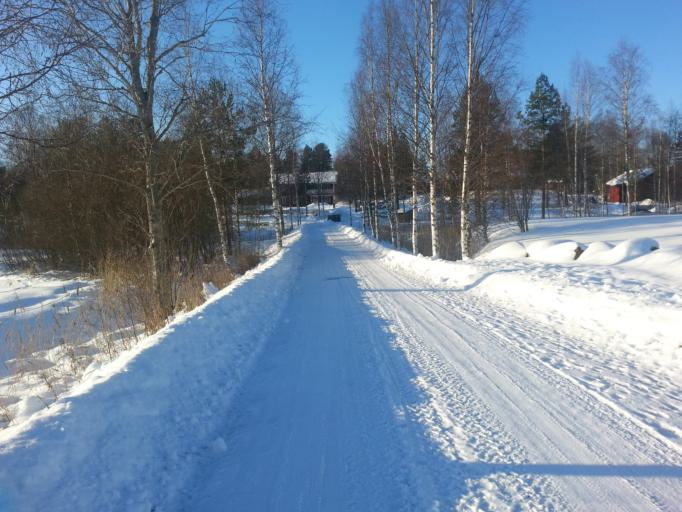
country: SE
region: Dalarna
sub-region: Borlange Kommun
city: Borlaenge
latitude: 60.5745
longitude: 15.4685
